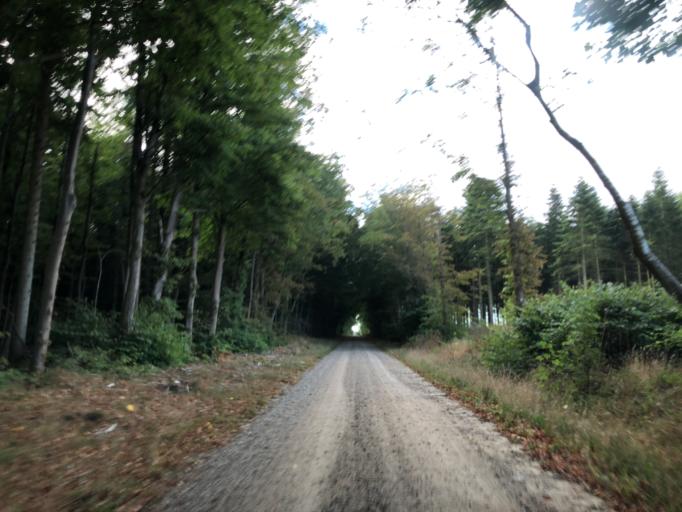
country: DK
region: Central Jutland
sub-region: Holstebro Kommune
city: Ulfborg
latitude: 56.1617
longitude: 8.4068
